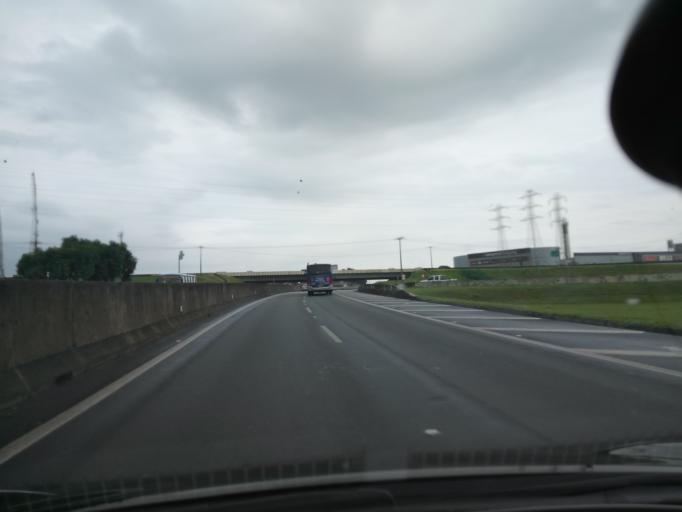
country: BR
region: Sao Paulo
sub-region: Campinas
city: Campinas
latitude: -22.9319
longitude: -47.0721
